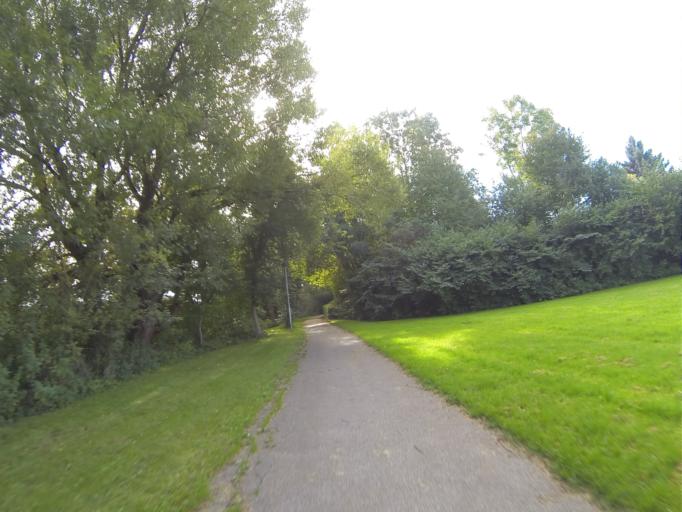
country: SE
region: Skane
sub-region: Eslovs Kommun
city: Eslov
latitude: 55.7253
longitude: 13.3494
